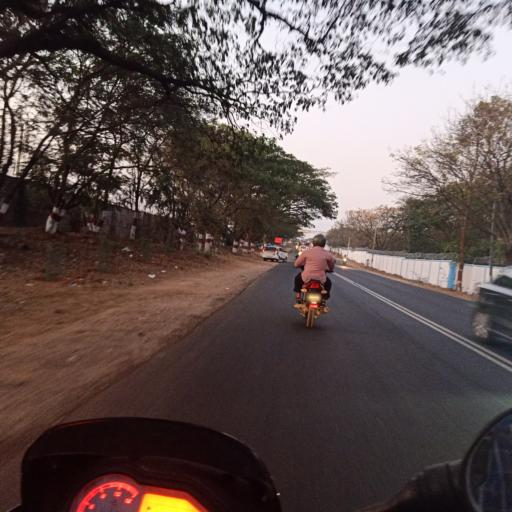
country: IN
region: Telangana
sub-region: Rangareddi
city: Secunderabad
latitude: 17.5516
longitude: 78.5360
